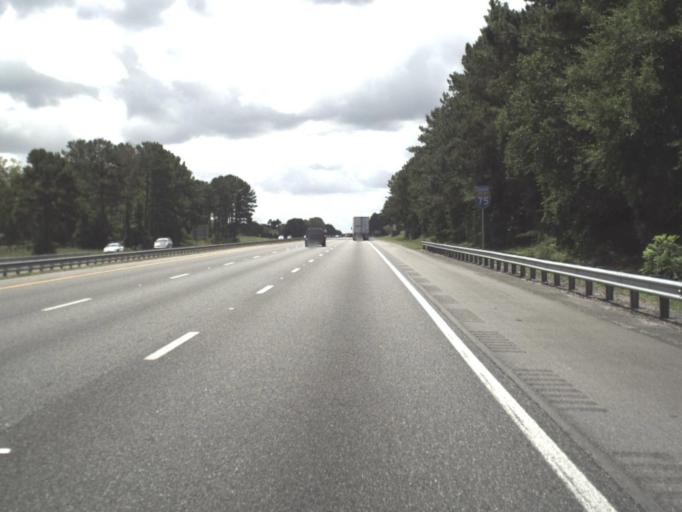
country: US
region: Florida
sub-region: Columbia County
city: Lake City
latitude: 30.1111
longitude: -82.6522
